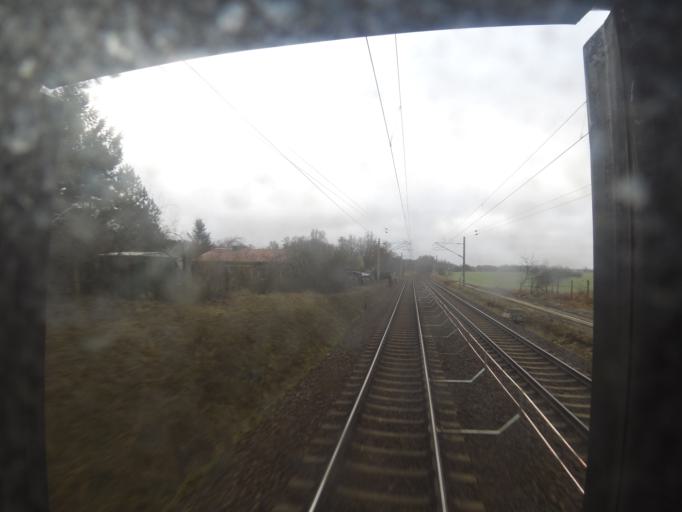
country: DE
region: Brandenburg
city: Rangsdorf
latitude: 52.2792
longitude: 13.4360
